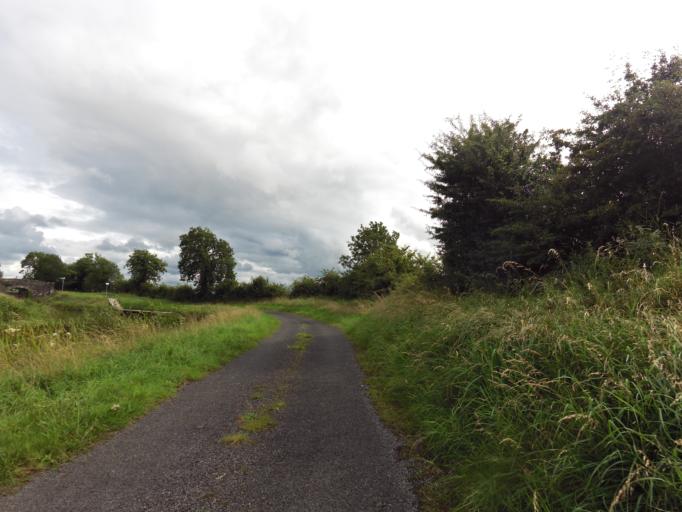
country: IE
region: Leinster
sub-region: An Iarmhi
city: An Muileann gCearr
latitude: 53.5588
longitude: -7.5020
